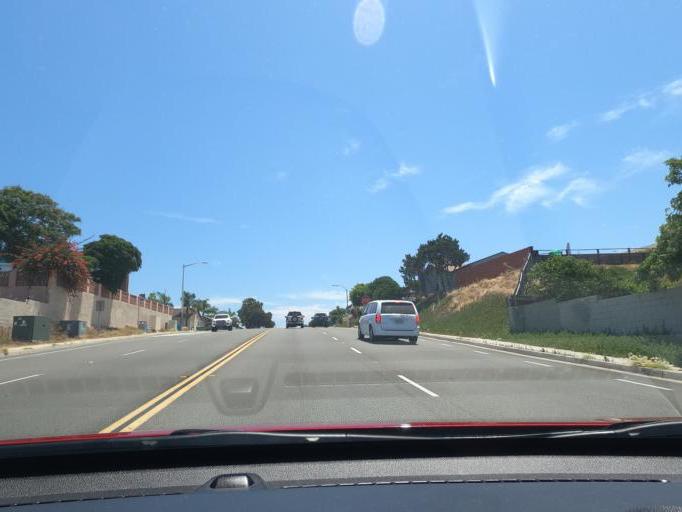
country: US
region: California
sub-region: San Diego County
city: Imperial Beach
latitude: 32.5736
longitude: -117.0506
